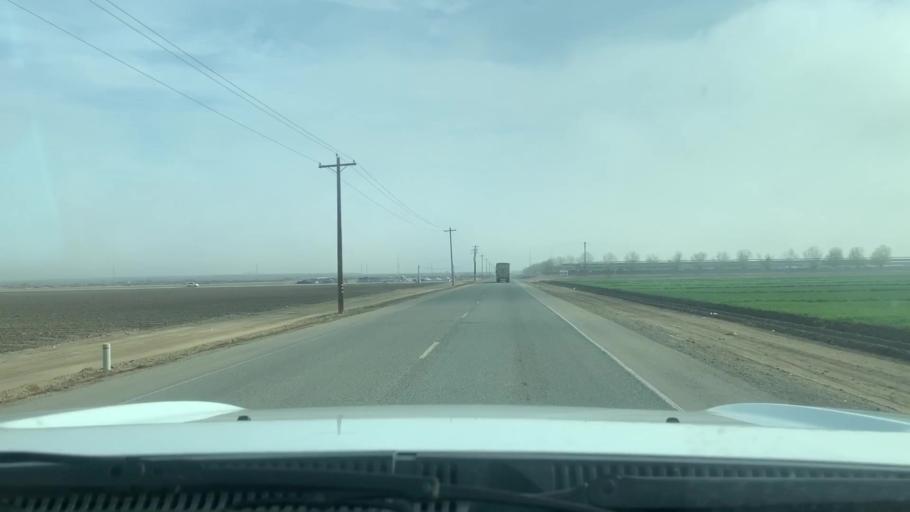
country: US
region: California
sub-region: Kern County
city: Buttonwillow
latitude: 35.5005
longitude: -119.4600
